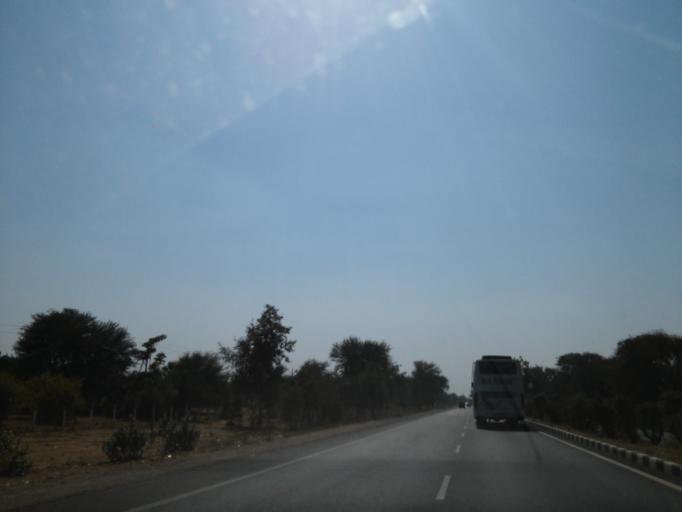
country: IN
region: Gujarat
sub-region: Gandhinagar
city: Chhala
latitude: 23.2833
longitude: 72.7610
